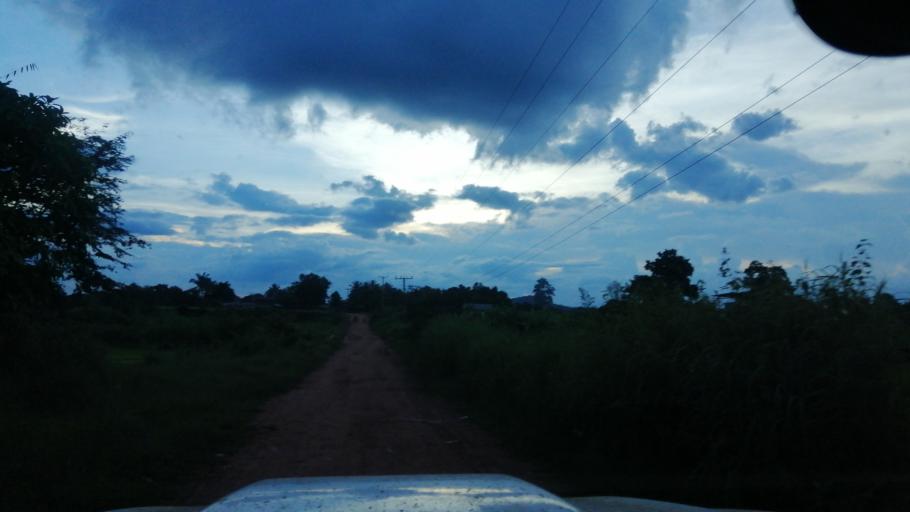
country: TH
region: Uttaradit
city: Ban Khok
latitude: 17.8778
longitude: 101.0519
